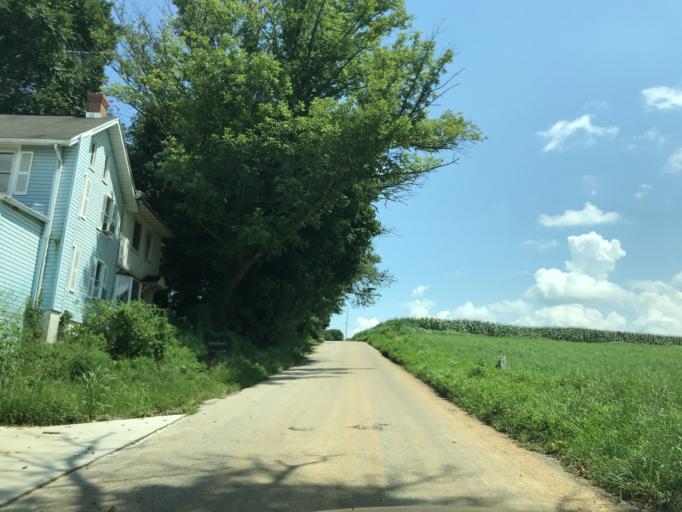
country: US
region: Pennsylvania
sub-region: York County
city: New Freedom
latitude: 39.7232
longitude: -76.7080
